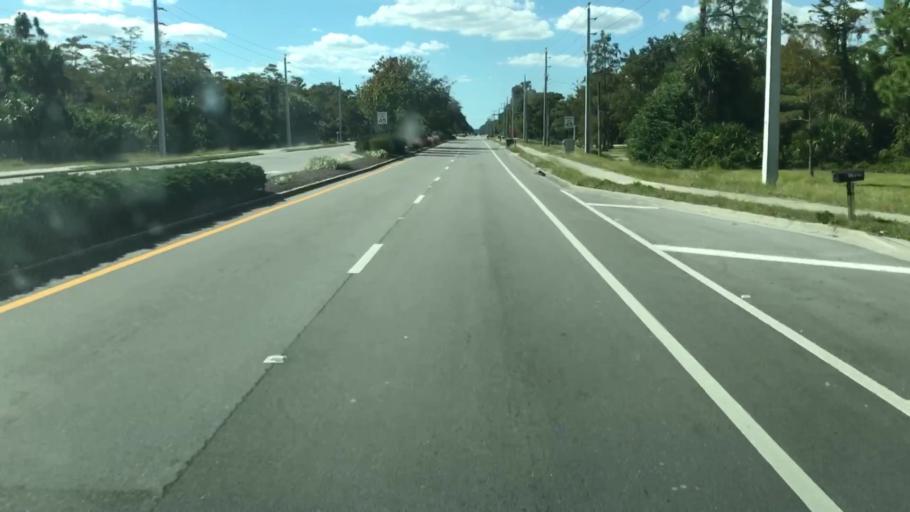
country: US
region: Florida
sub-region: Collier County
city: Vineyards
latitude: 26.2294
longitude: -81.6454
